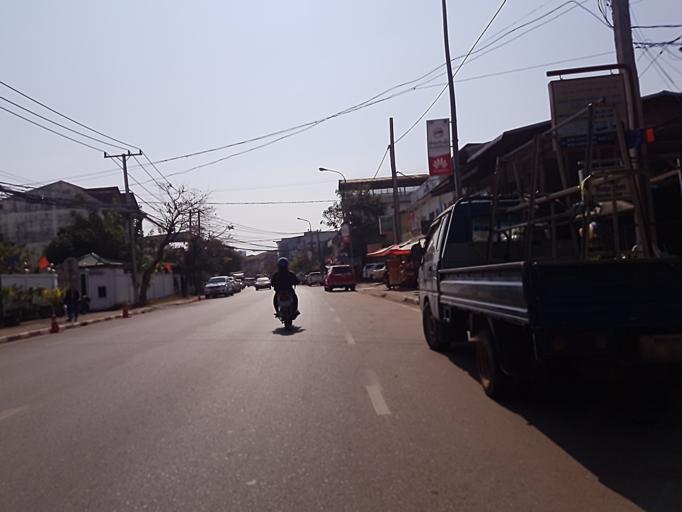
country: LA
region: Vientiane
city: Vientiane
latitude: 17.9724
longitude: 102.6302
